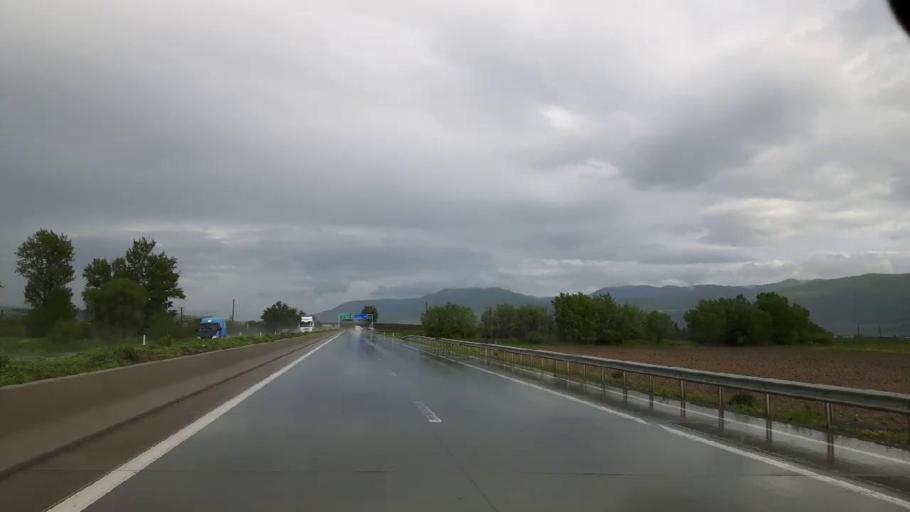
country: GE
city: Agara
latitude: 42.0345
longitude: 43.9424
